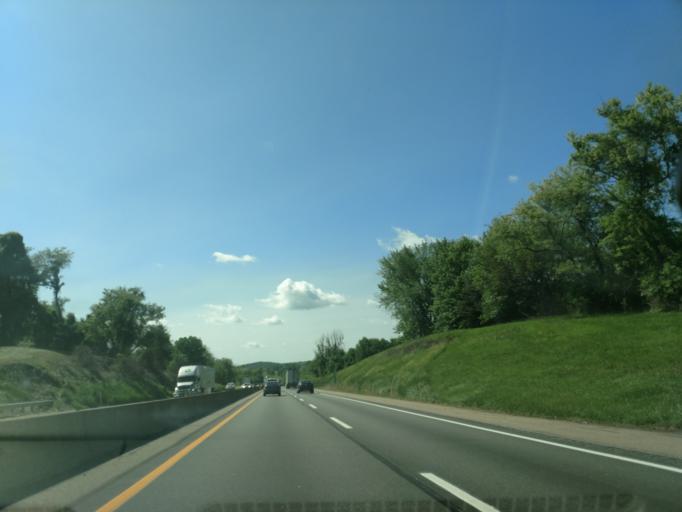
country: US
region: Pennsylvania
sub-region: Chester County
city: Downingtown
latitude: 40.0769
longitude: -75.6997
